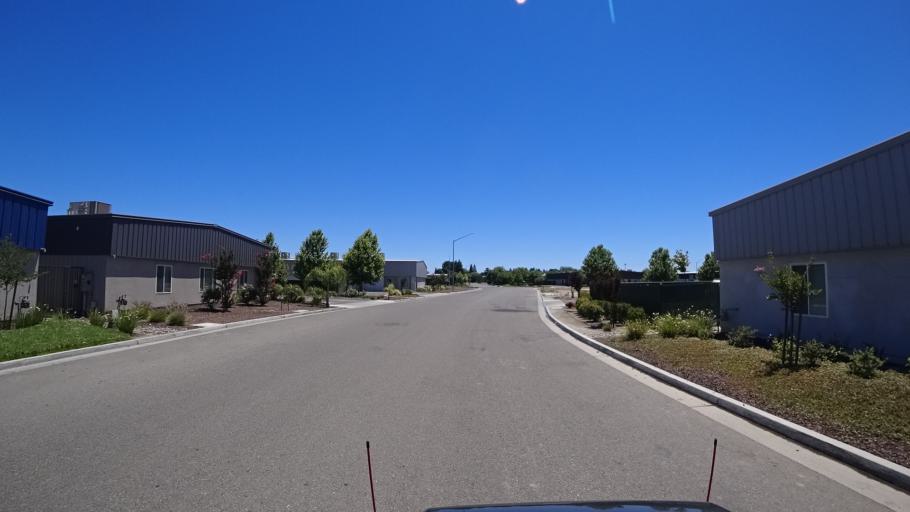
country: US
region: California
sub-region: Fresno County
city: West Park
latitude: 36.7978
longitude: -119.8598
